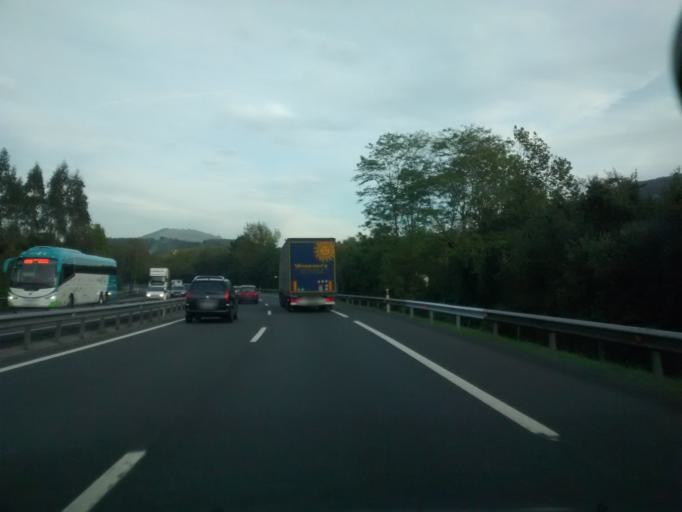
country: ES
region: Basque Country
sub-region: Provincia de Guipuzcoa
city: Cestona
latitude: 43.2594
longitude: -2.2874
